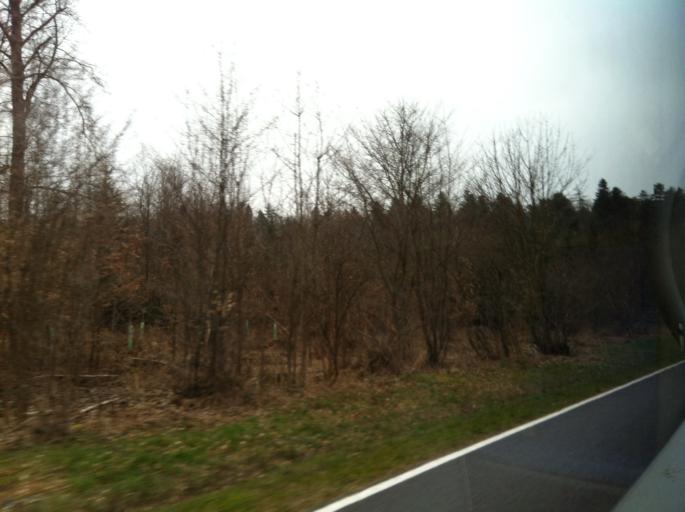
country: DE
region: Baden-Wuerttemberg
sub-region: Karlsruhe Region
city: Limbach
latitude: 49.4585
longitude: 9.1917
